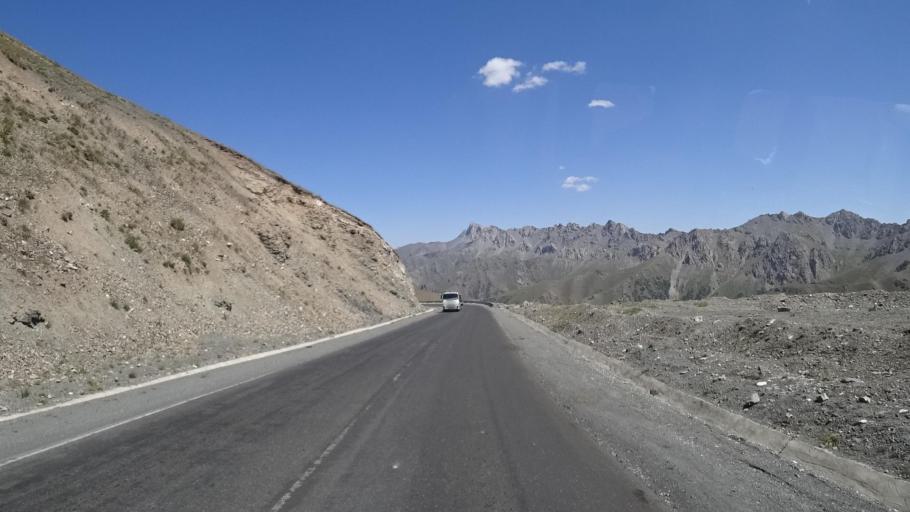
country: KG
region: Osh
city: Gul'cha
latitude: 39.7723
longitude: 73.1717
